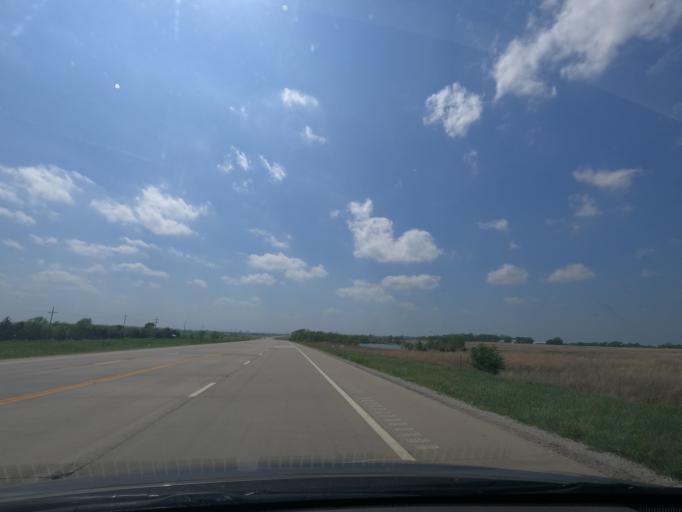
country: US
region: Kansas
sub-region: Elk County
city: Howard
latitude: 37.6360
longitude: -96.1732
